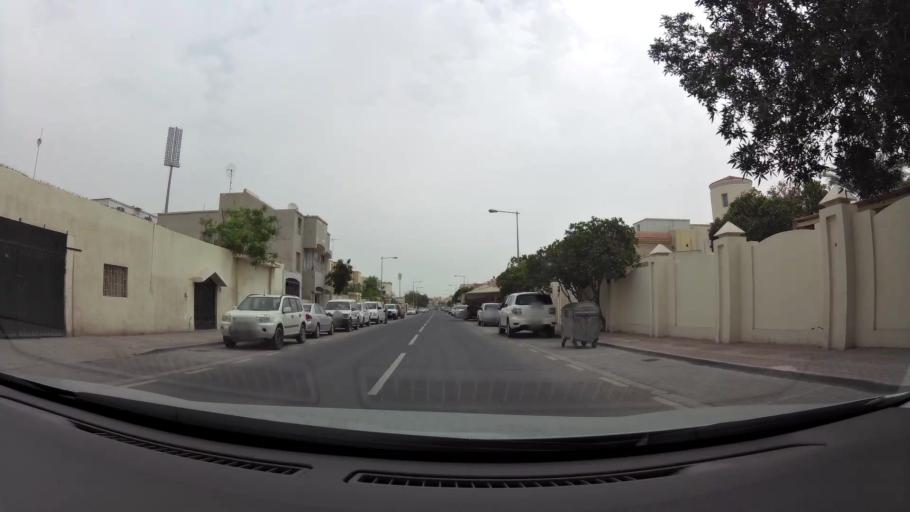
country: QA
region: Baladiyat ad Dawhah
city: Doha
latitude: 25.2569
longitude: 51.5186
